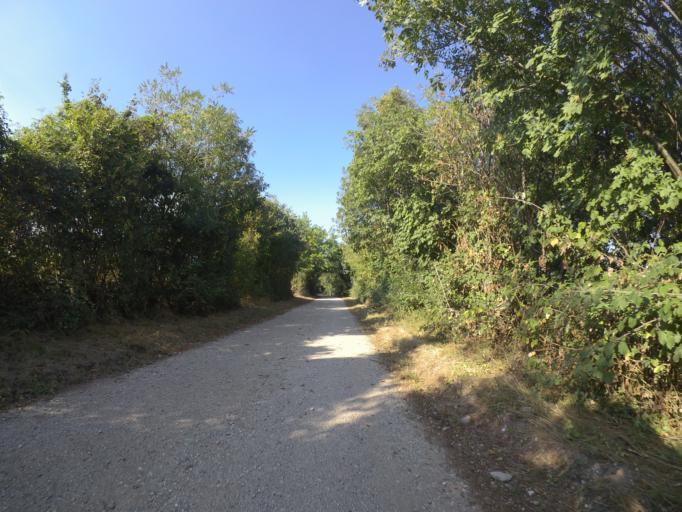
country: IT
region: Friuli Venezia Giulia
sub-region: Provincia di Udine
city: Pozzuolo del Friuli
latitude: 46.0094
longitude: 13.1876
